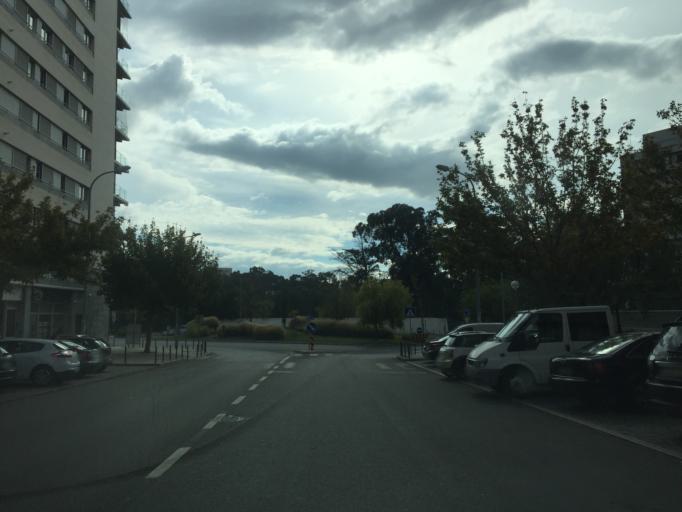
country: PT
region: Lisbon
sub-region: Odivelas
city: Olival do Basto
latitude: 38.7722
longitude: -9.1535
